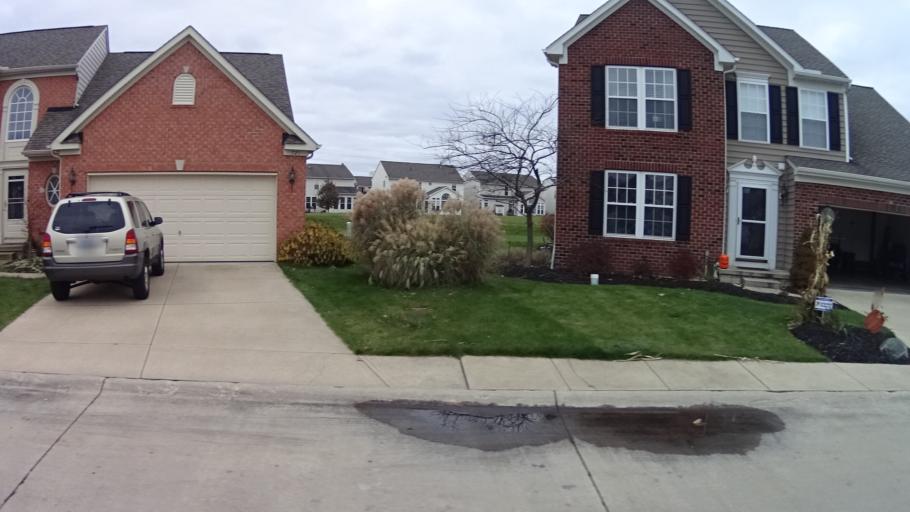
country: US
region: Ohio
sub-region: Cuyahoga County
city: Bay Village
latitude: 41.4803
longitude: -81.9708
